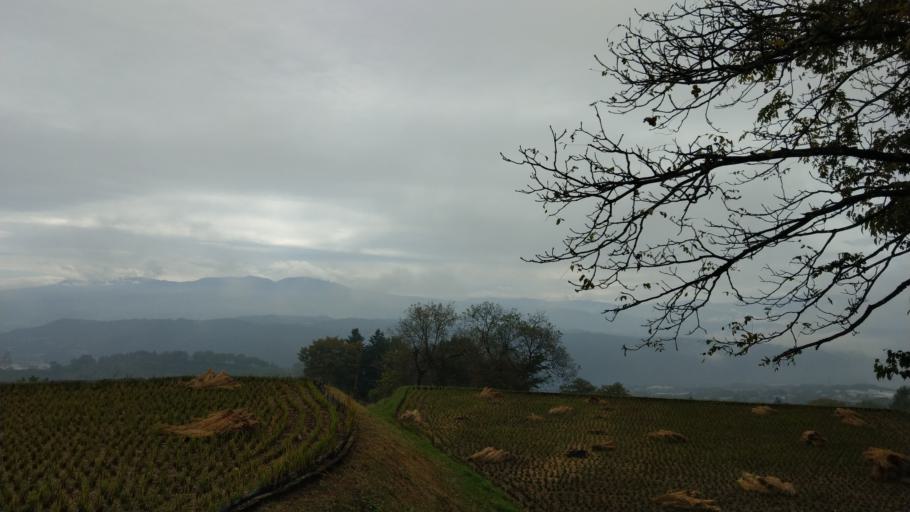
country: JP
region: Nagano
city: Komoro
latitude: 36.3549
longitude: 138.4210
